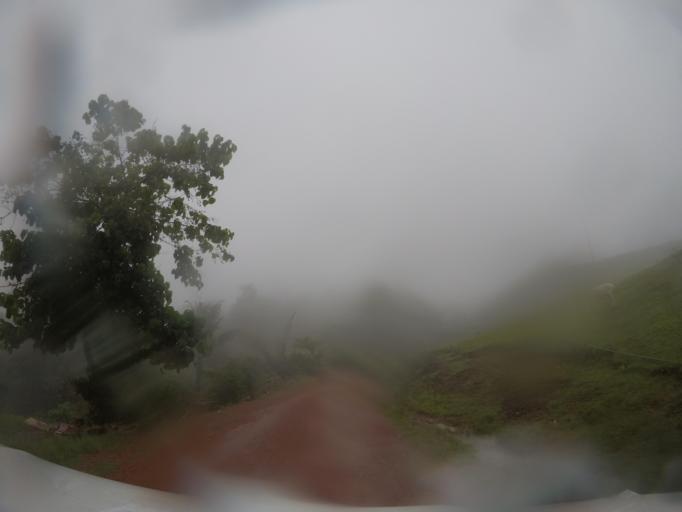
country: TL
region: Baucau
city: Venilale
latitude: -8.6389
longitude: 126.4160
